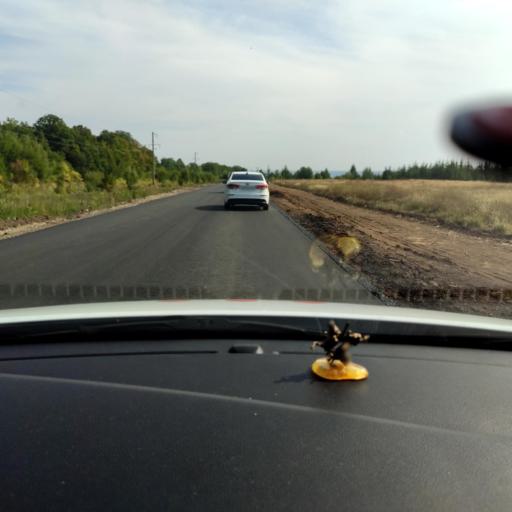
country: RU
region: Tatarstan
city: Verkhniy Uslon
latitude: 55.7362
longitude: 48.9513
